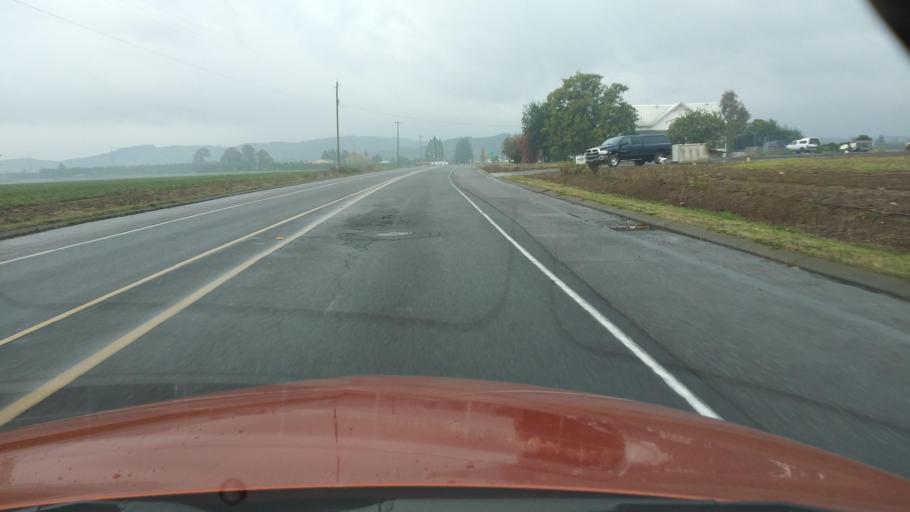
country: US
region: Oregon
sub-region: Washington County
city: Cornelius
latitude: 45.5514
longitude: -123.0676
